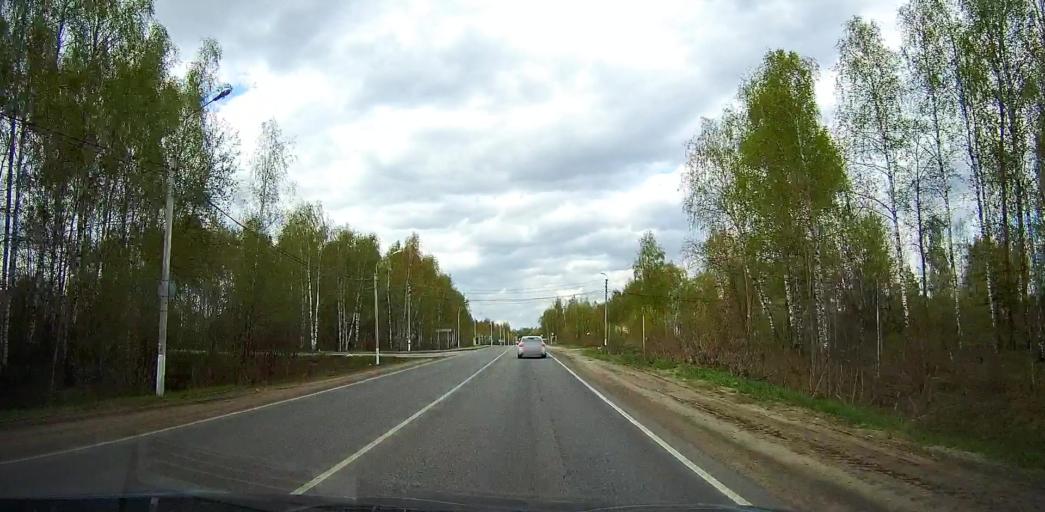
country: RU
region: Moskovskaya
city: Pavlovskiy Posad
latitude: 55.7576
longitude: 38.6559
